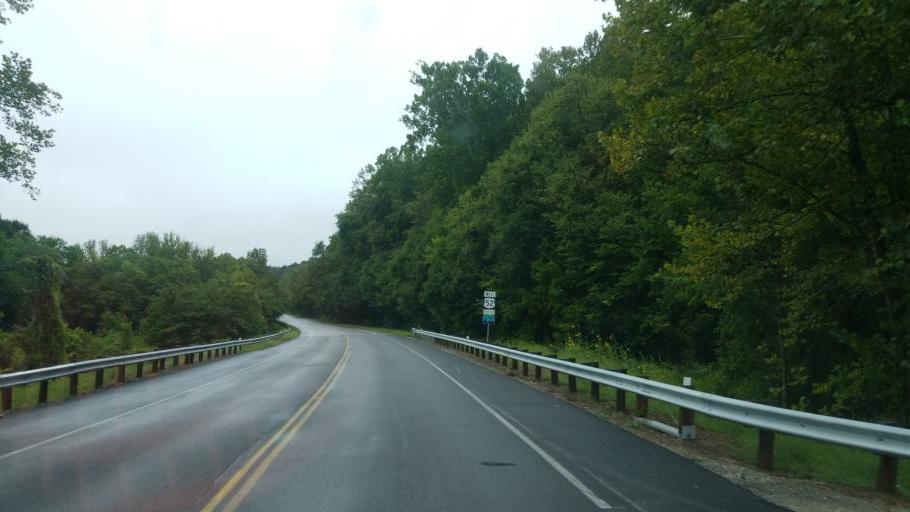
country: US
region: Ohio
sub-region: Adams County
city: Manchester
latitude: 38.6820
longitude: -83.6299
